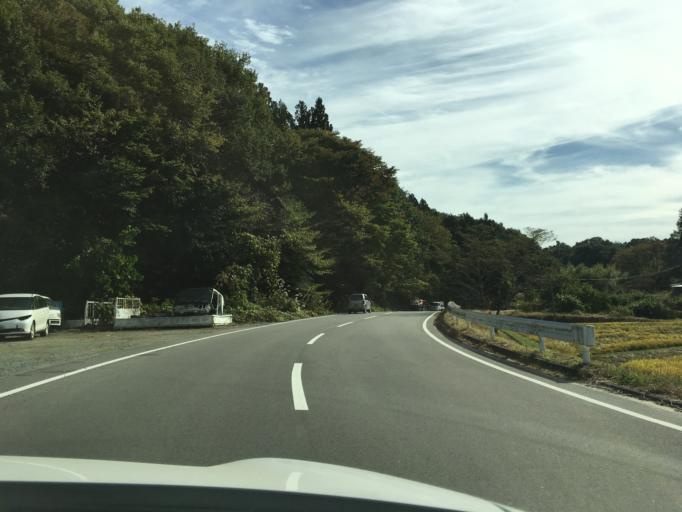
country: JP
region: Fukushima
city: Nihommatsu
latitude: 37.5324
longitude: 140.5072
